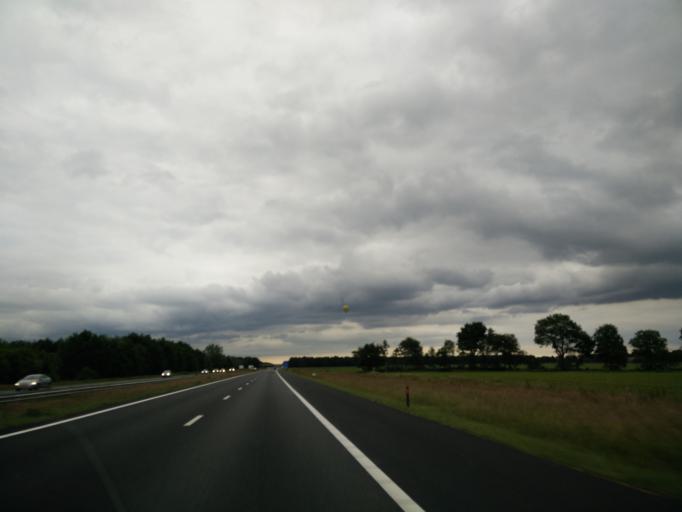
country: NL
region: Drenthe
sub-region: Gemeente Assen
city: Assen
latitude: 52.9358
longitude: 6.5374
